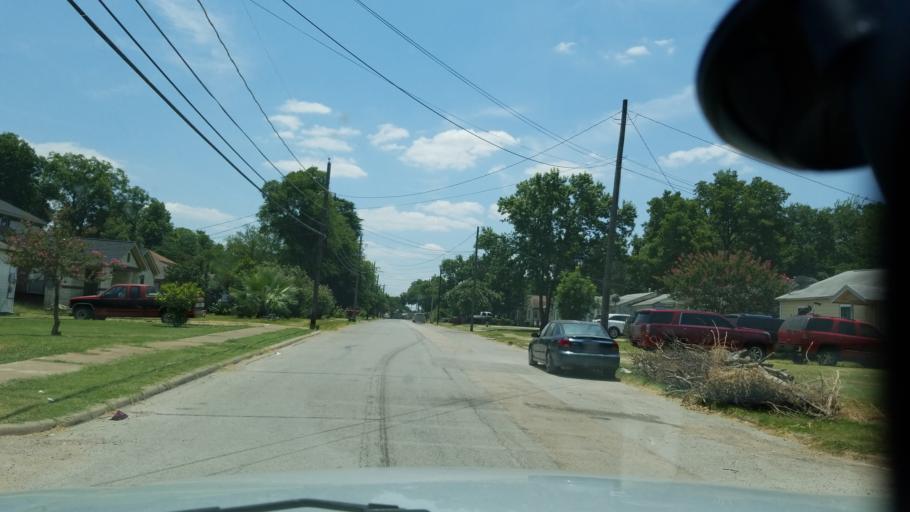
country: US
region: Texas
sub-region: Dallas County
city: Grand Prairie
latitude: 32.7524
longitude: -96.9617
